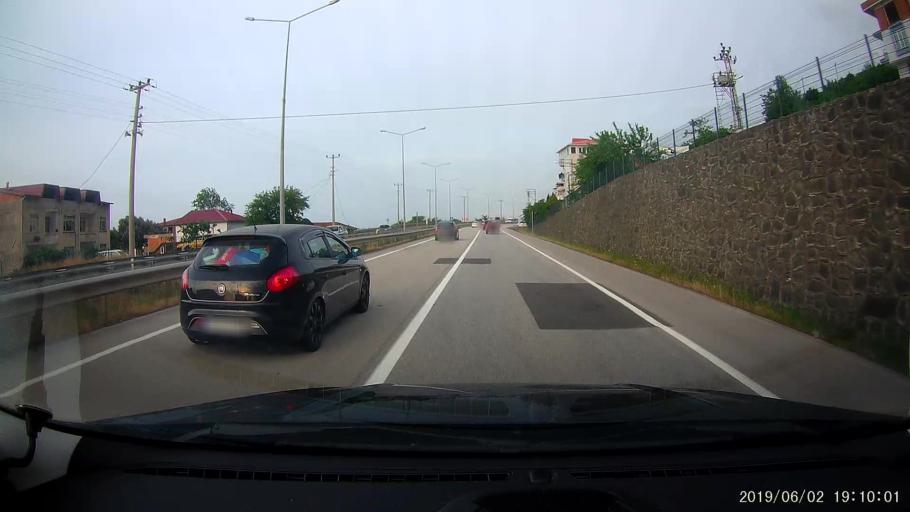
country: TR
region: Ordu
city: Gulyali
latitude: 40.9716
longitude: 38.0380
